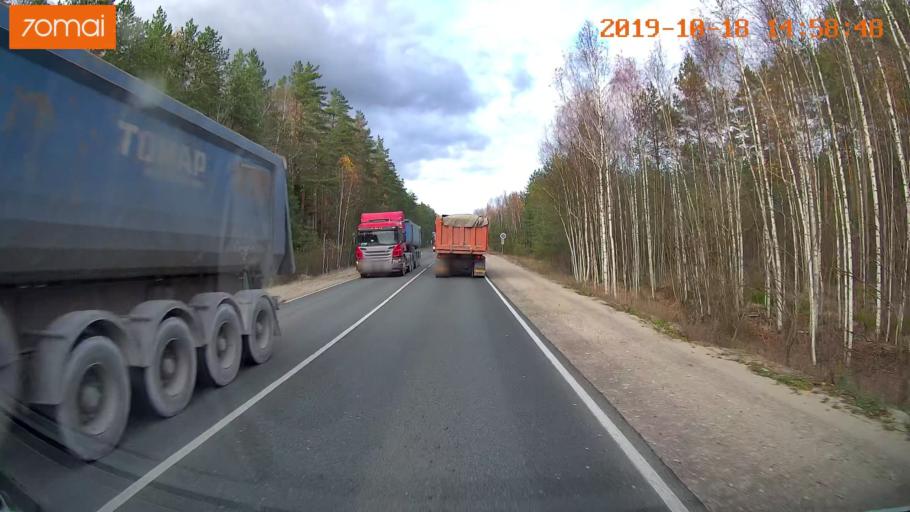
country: RU
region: Vladimir
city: Kurlovo
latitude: 55.4939
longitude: 40.5757
